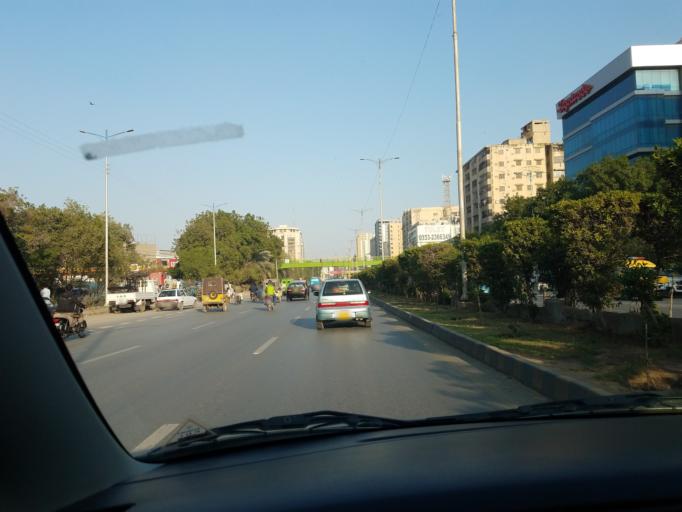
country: PK
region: Sindh
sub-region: Karachi District
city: Karachi
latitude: 24.8599
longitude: 67.0608
